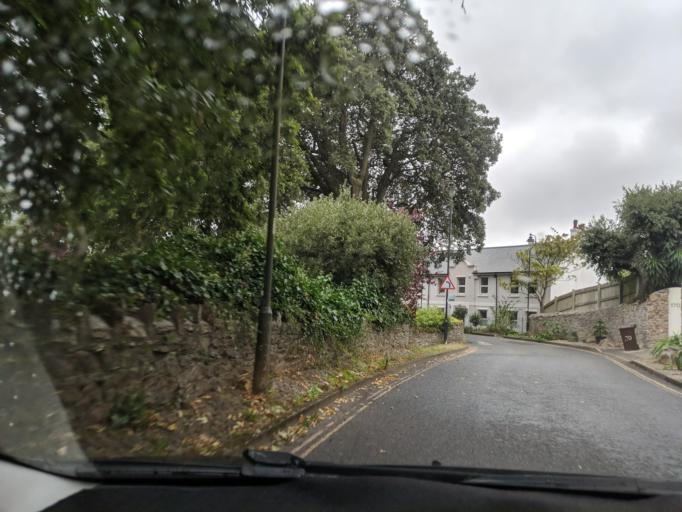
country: GB
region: England
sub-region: Plymouth
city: Plymouth
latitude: 50.3623
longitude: -4.1611
